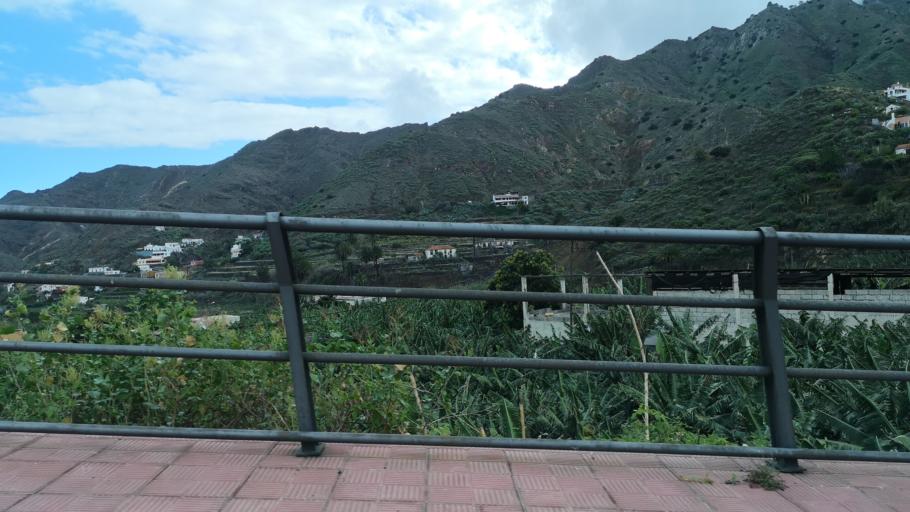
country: ES
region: Canary Islands
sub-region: Provincia de Santa Cruz de Tenerife
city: Hermigua
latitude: 28.1692
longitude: -17.1918
